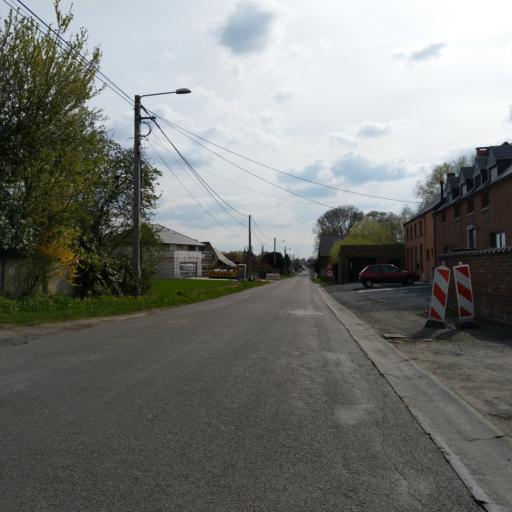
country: BE
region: Wallonia
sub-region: Province du Hainaut
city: Jurbise
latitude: 50.5235
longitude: 3.9640
